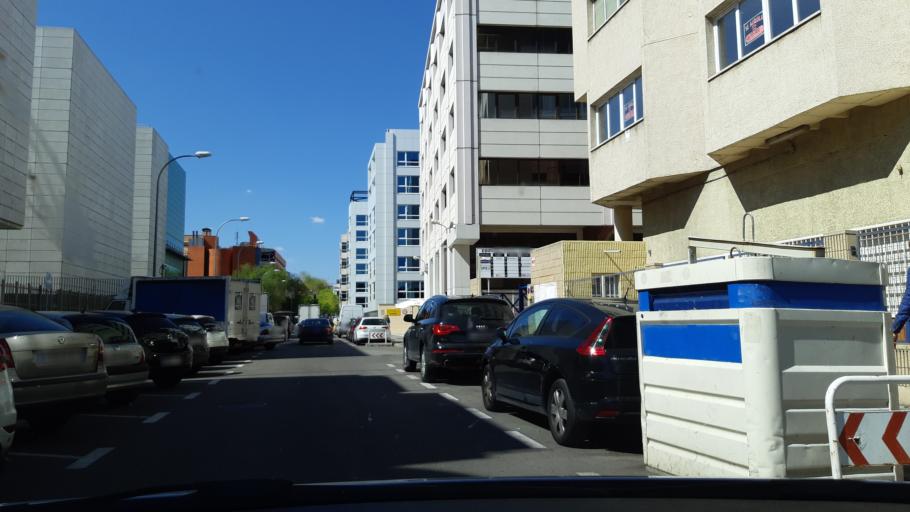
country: ES
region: Madrid
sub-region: Provincia de Madrid
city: San Blas
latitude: 40.4332
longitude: -3.6285
